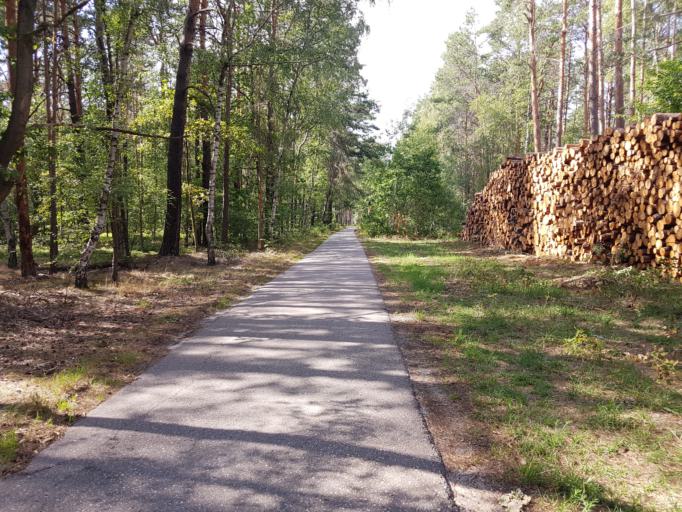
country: DE
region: Brandenburg
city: Finsterwalde
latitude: 51.6213
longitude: 13.6691
